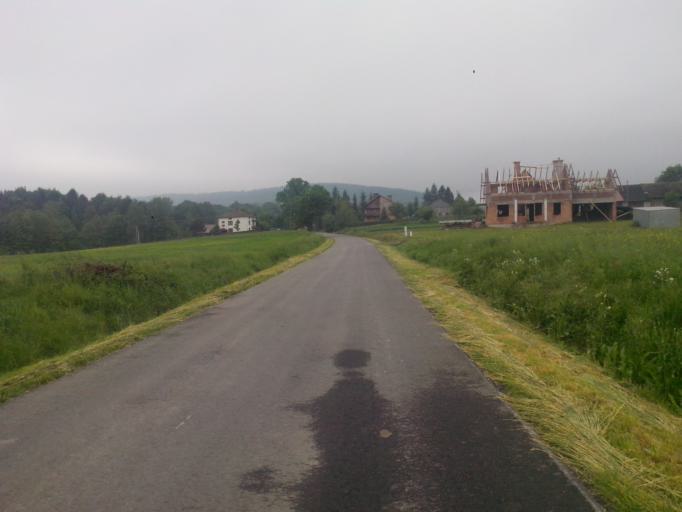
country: PL
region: Subcarpathian Voivodeship
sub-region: Powiat strzyzowski
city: Strzyzow
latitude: 49.8459
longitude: 21.7767
